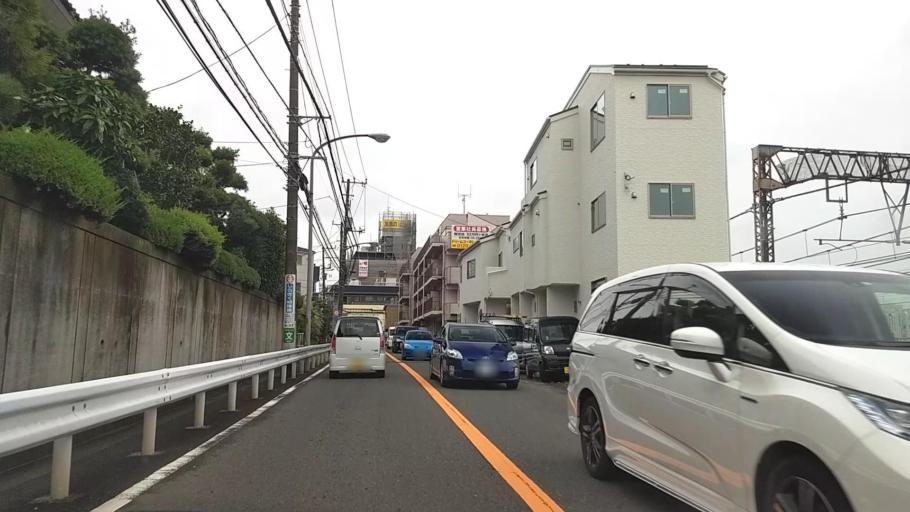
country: JP
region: Kanagawa
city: Fujisawa
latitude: 35.3898
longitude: 139.5356
